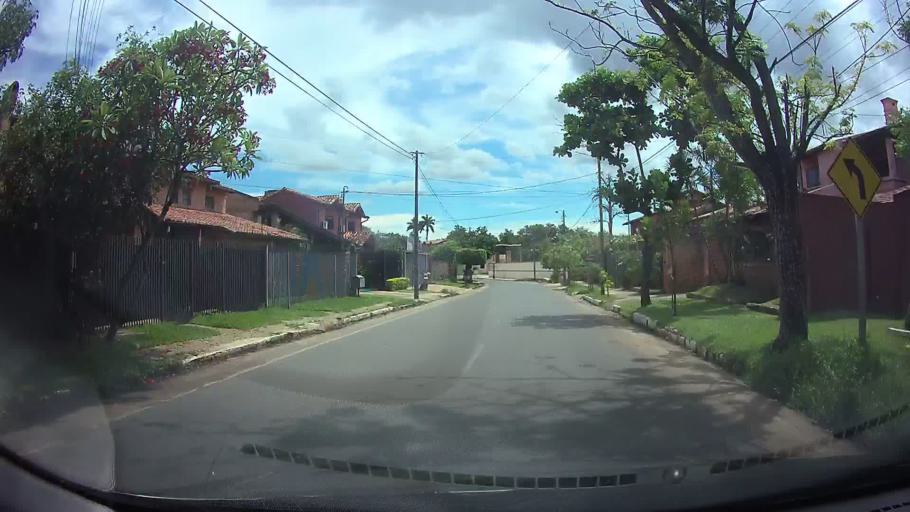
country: PY
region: Central
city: Fernando de la Mora
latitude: -25.3179
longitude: -57.5277
